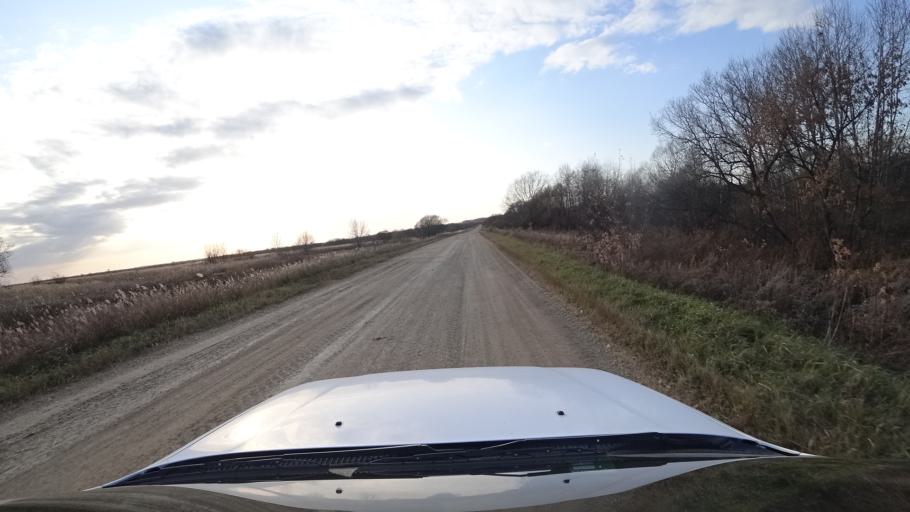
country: RU
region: Primorskiy
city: Lazo
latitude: 45.8255
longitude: 133.6067
